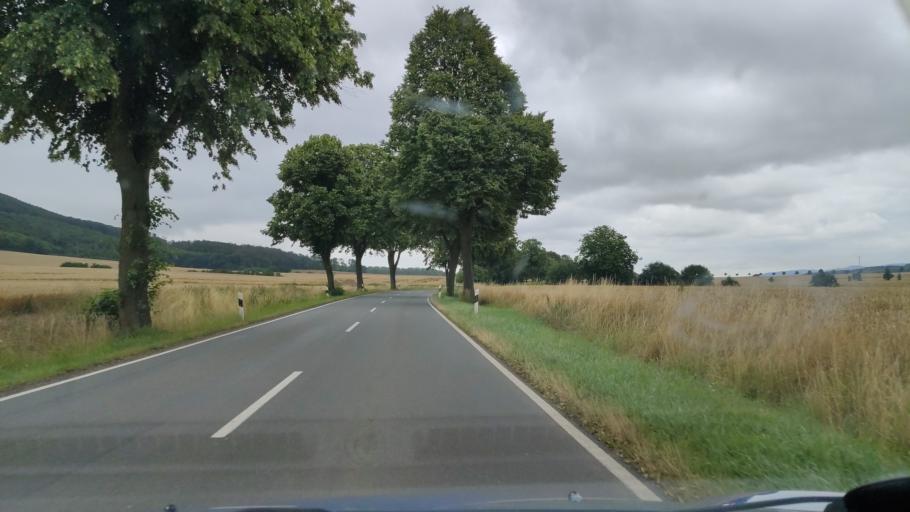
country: DE
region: Lower Saxony
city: Coppenbrugge
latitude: 52.0764
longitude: 9.5116
